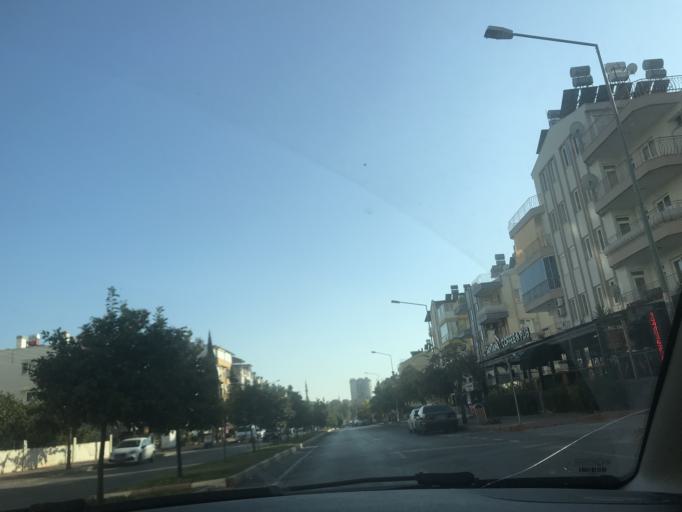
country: TR
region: Antalya
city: Antalya
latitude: 36.8867
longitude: 30.6472
